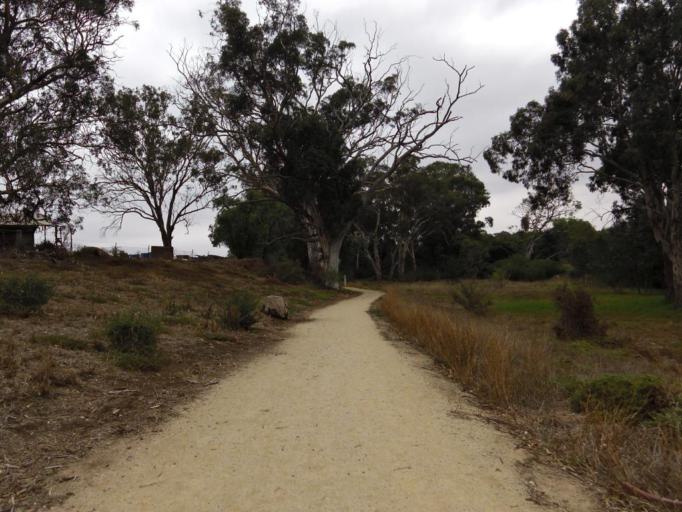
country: AU
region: Victoria
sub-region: Moorabool
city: Bacchus Marsh
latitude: -37.6565
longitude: 144.4503
